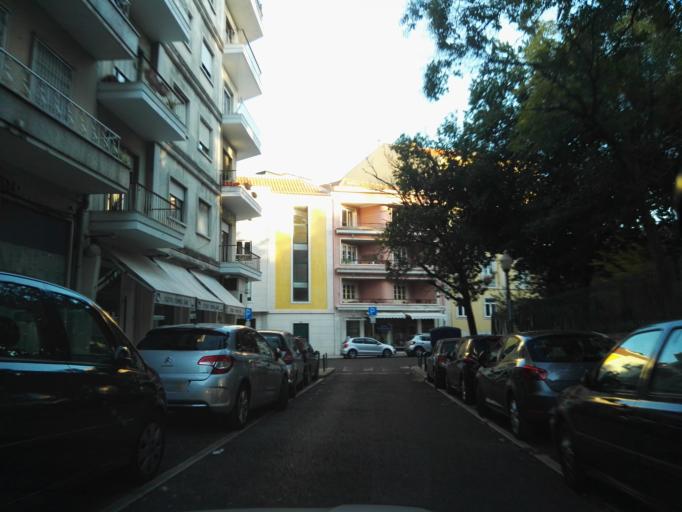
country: PT
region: Lisbon
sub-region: Lisbon
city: Lisbon
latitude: 38.7153
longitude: -9.1577
